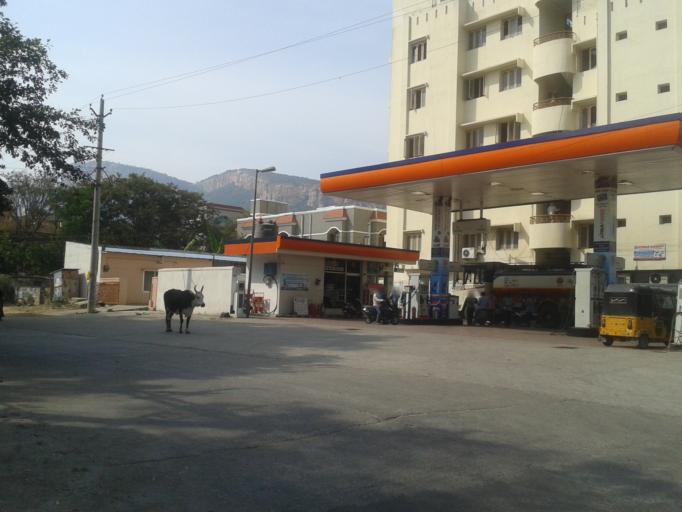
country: IN
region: Andhra Pradesh
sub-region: Chittoor
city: Tirupati
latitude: 13.6426
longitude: 79.4187
